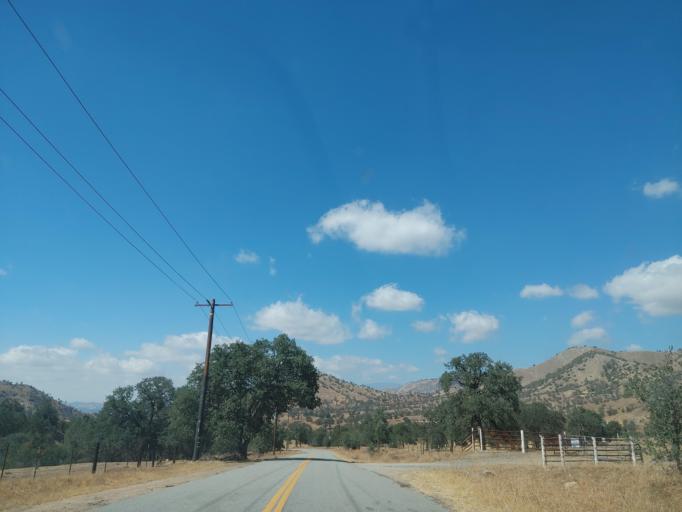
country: US
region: California
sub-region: Kern County
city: Golden Hills
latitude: 35.2031
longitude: -118.5425
